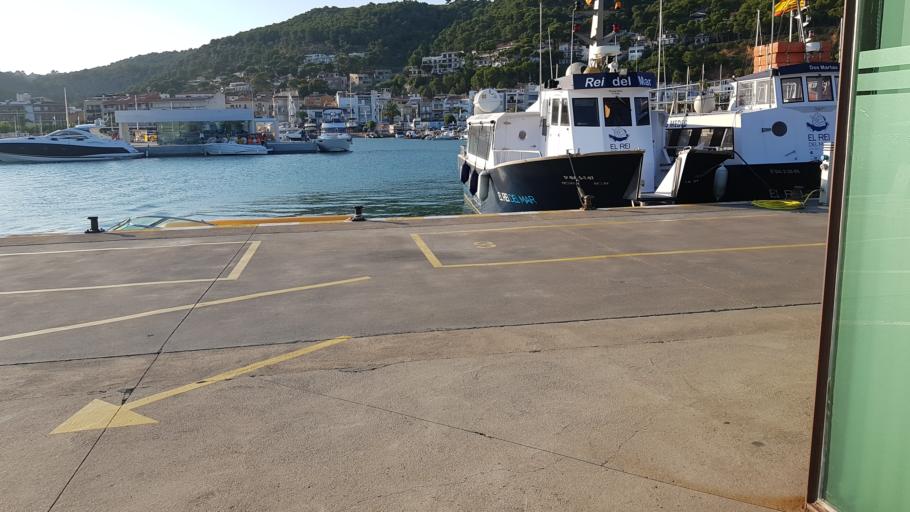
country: ES
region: Catalonia
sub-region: Provincia de Girona
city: Torroella de Montgri
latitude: 42.0524
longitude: 3.2041
